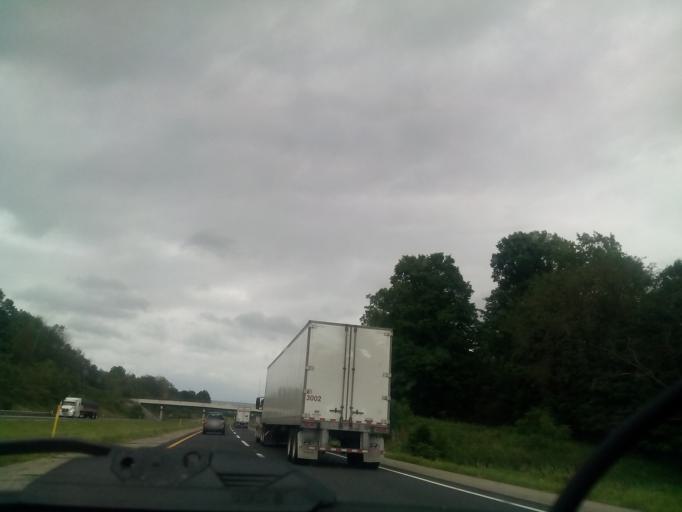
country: US
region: Indiana
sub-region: Steuben County
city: Hamilton
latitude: 41.6411
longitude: -84.8320
